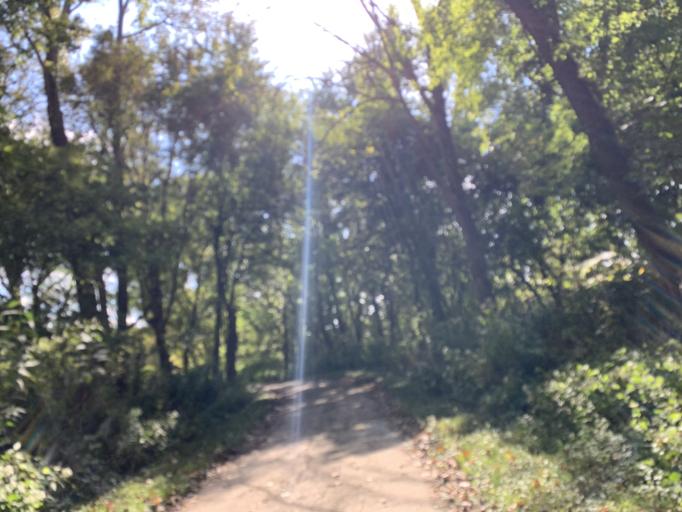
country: US
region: Indiana
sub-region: Floyd County
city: New Albany
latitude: 38.2644
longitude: -85.8302
